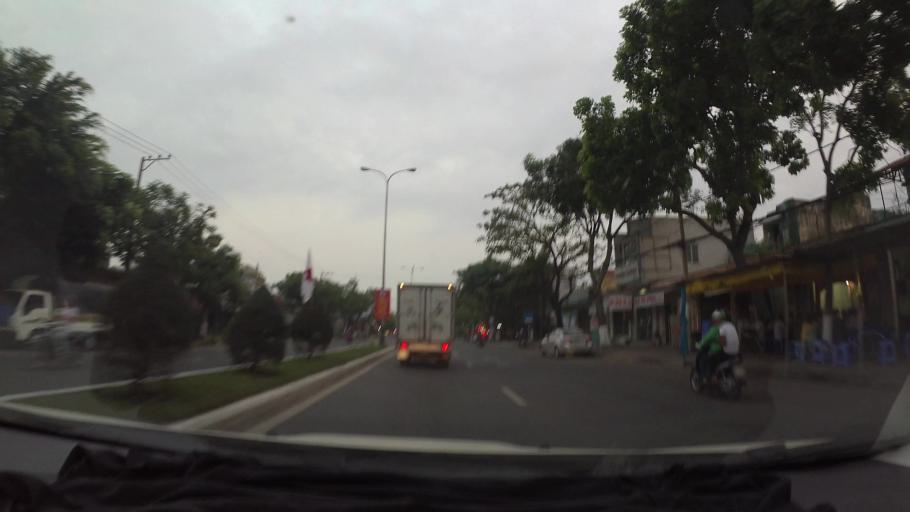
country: VN
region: Da Nang
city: Lien Chieu
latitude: 16.0800
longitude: 108.1471
